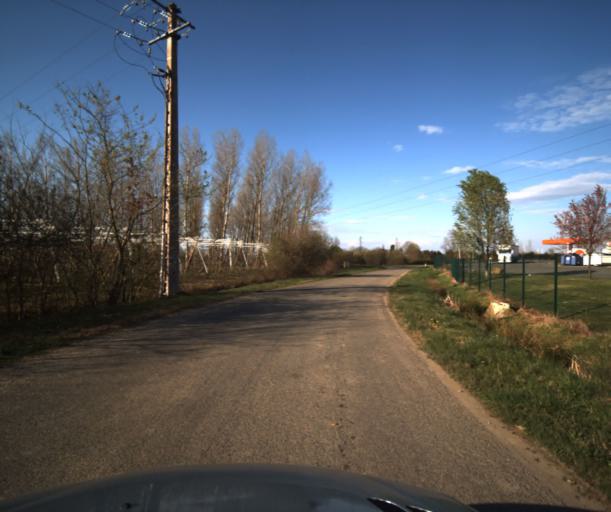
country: FR
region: Midi-Pyrenees
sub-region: Departement du Tarn-et-Garonne
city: Bressols
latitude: 43.9574
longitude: 1.3257
